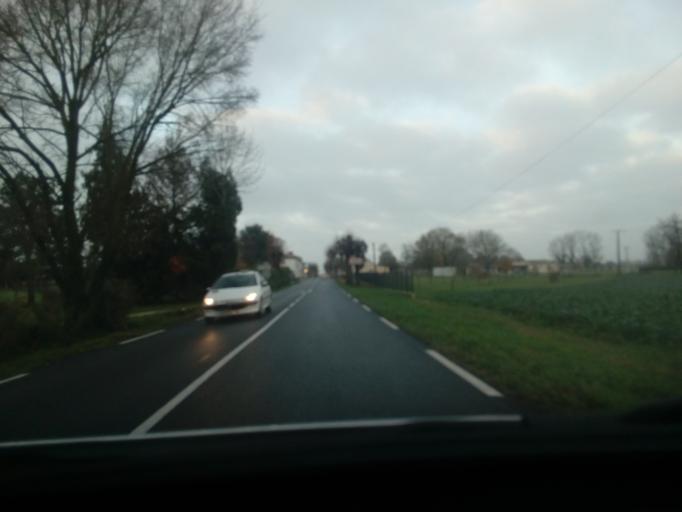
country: FR
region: Poitou-Charentes
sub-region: Departement de la Charente
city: Baignes-Sainte-Radegonde
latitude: 45.4434
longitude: -0.2961
